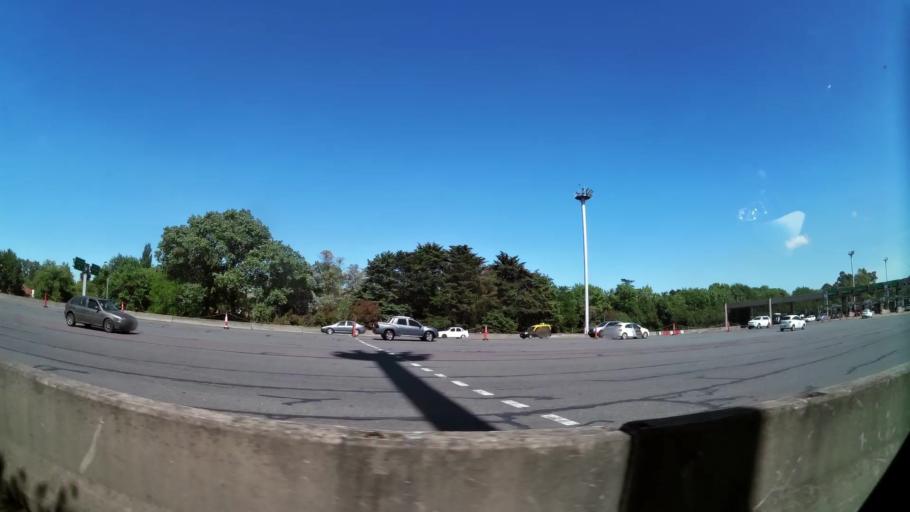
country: AR
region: Buenos Aires
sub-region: Partido de San Isidro
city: San Isidro
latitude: -34.4869
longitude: -58.5589
